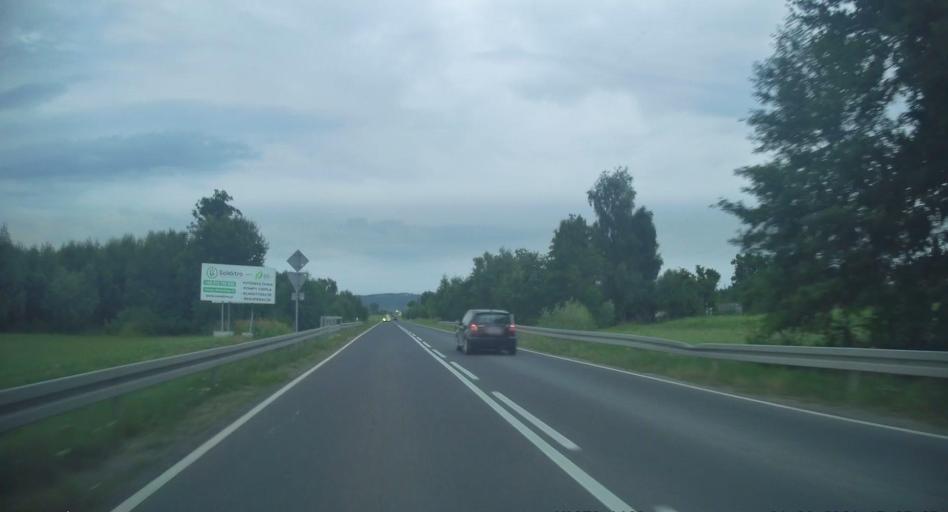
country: PL
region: Lesser Poland Voivodeship
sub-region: Powiat tarnowski
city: Wojnicz
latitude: 49.9728
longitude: 20.8443
